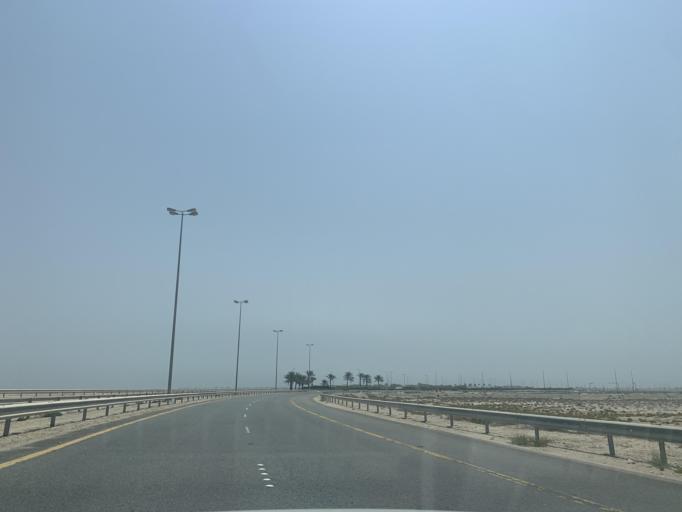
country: BH
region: Central Governorate
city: Dar Kulayb
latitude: 25.8488
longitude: 50.5895
